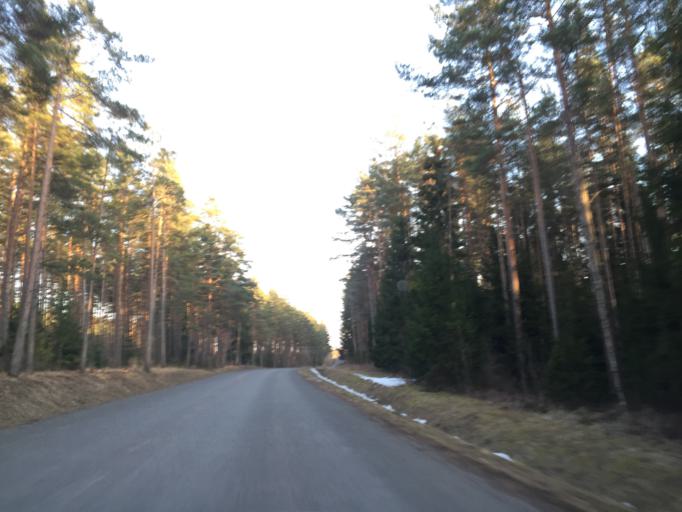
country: EE
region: Laeaene
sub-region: Lihula vald
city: Lihula
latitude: 58.4690
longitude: 23.7171
